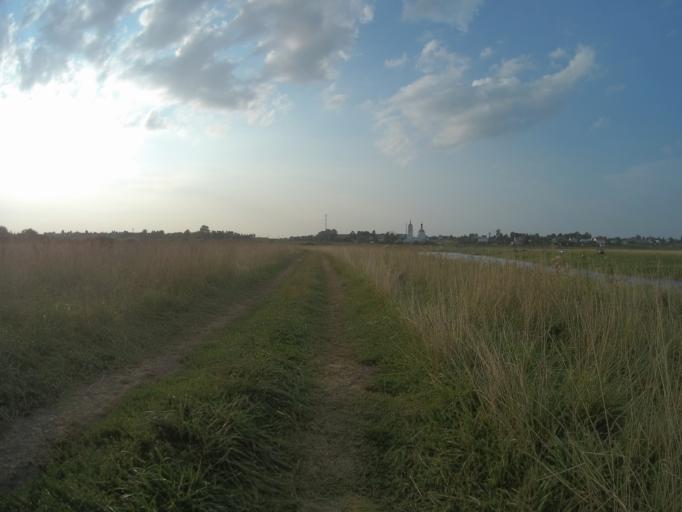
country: RU
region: Vladimir
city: Orgtrud
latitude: 56.3022
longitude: 40.6096
